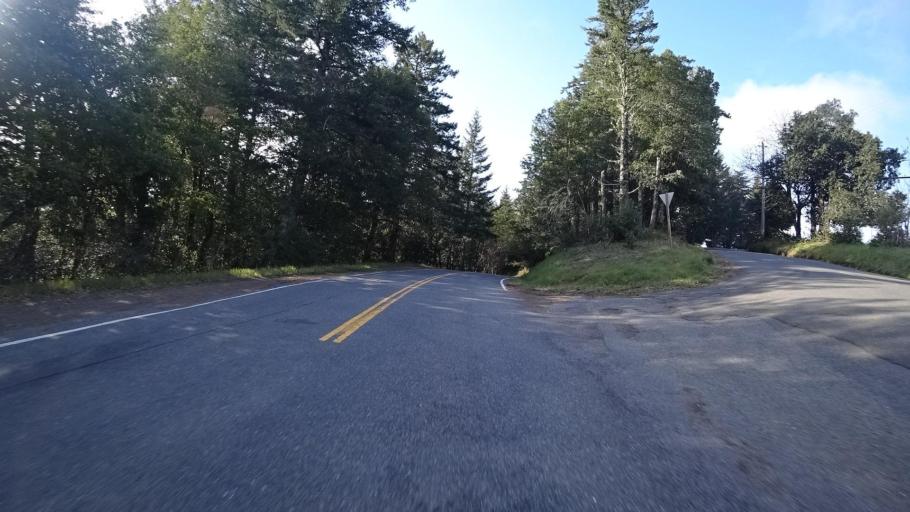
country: US
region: California
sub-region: Humboldt County
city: Blue Lake
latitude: 40.7248
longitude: -123.9446
